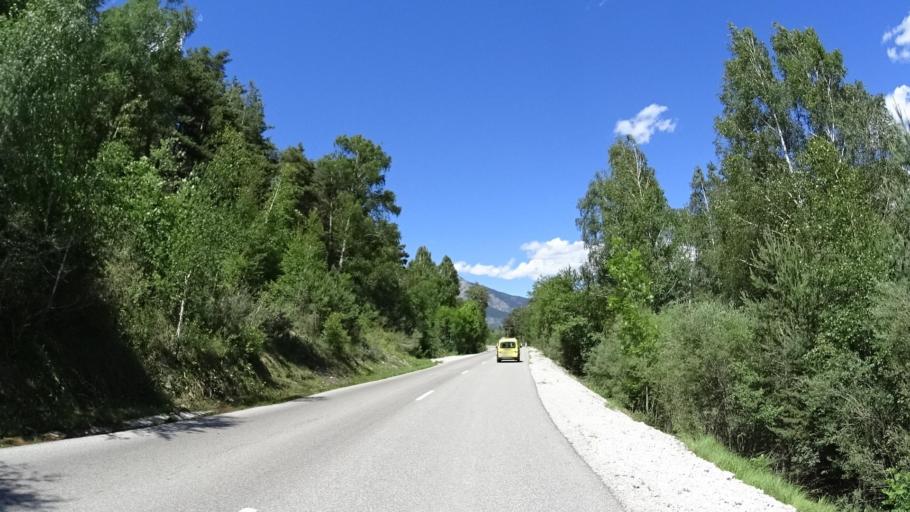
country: FR
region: Provence-Alpes-Cote d'Azur
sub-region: Departement des Alpes-de-Haute-Provence
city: Annot
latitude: 44.1201
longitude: 6.5796
